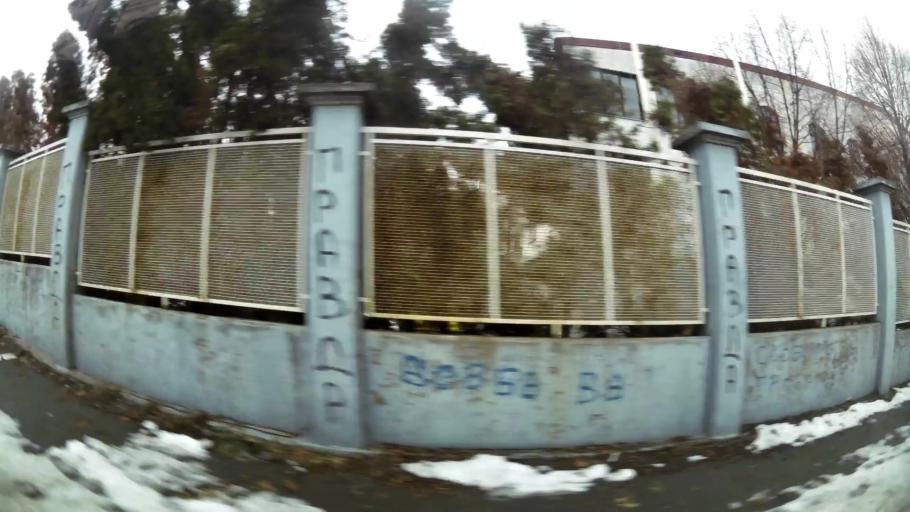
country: RS
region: Central Serbia
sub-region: Belgrade
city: Vozdovac
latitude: 44.7543
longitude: 20.4995
